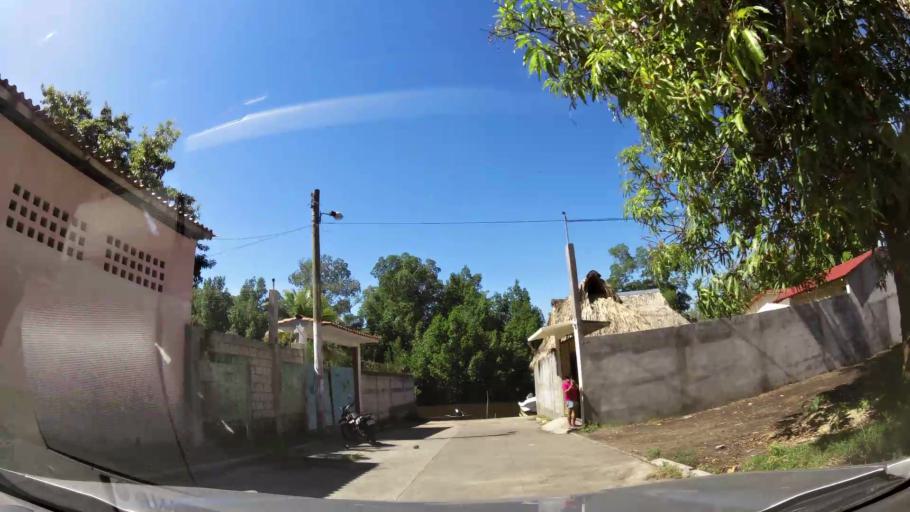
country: GT
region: Escuintla
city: Iztapa
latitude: 13.9320
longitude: -90.7184
